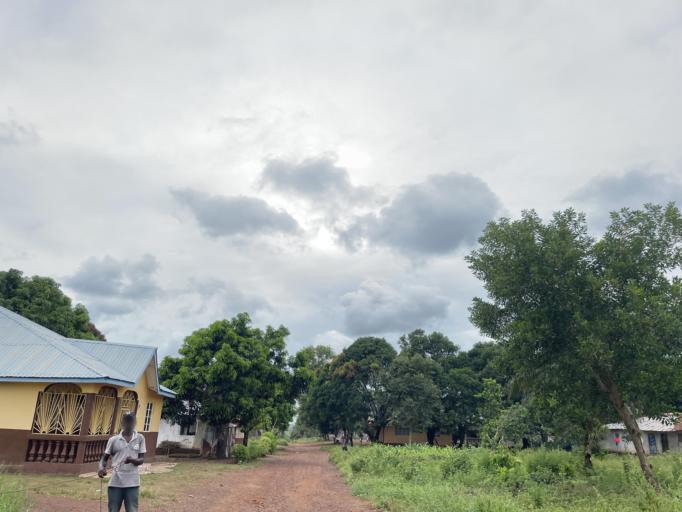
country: SL
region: Northern Province
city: Kambia
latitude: 9.1308
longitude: -12.9102
